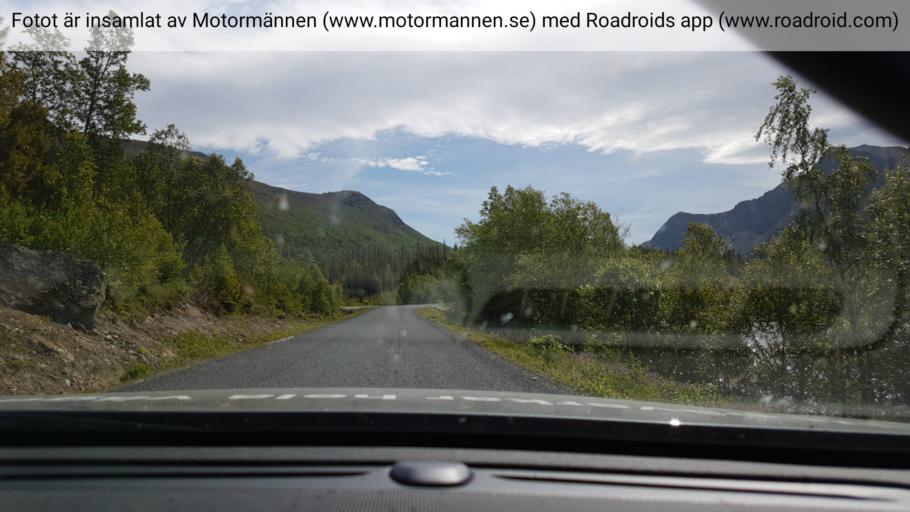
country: SE
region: Vaesterbotten
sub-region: Vilhelmina Kommun
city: Sjoberg
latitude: 65.2547
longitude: 15.4150
